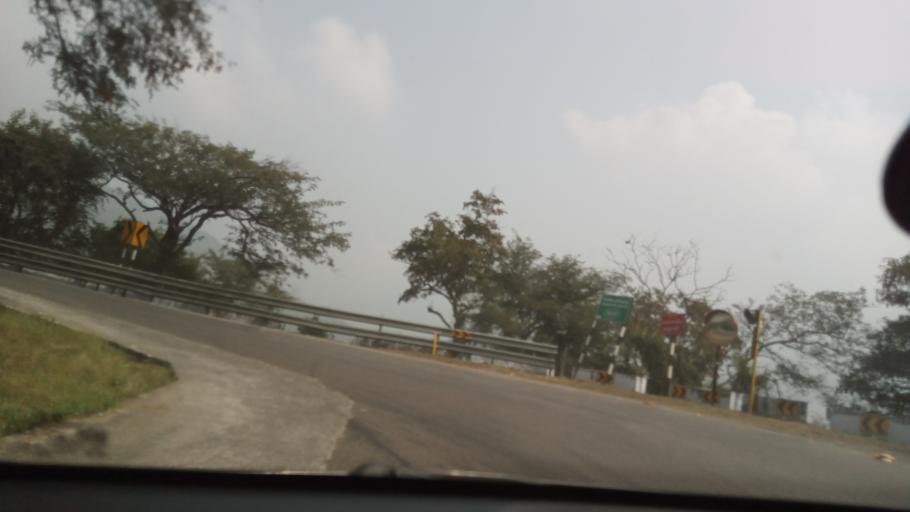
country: IN
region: Tamil Nadu
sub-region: Erode
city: Sathyamangalam
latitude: 11.5897
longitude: 77.1294
